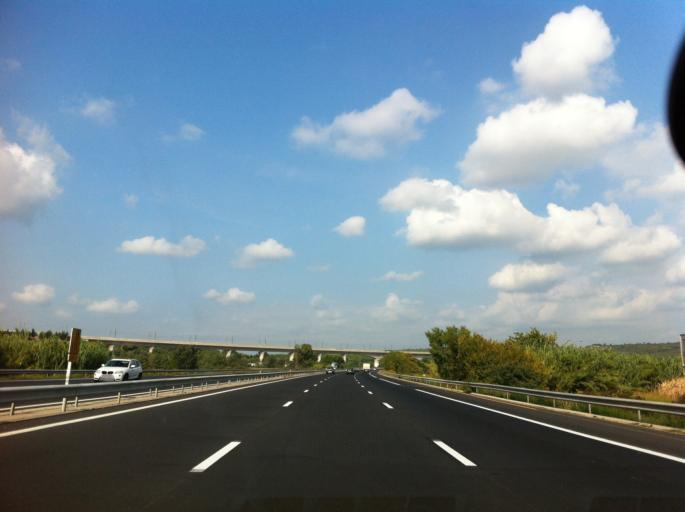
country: FR
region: Provence-Alpes-Cote d'Azur
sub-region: Departement des Bouches-du-Rhone
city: Eguilles
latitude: 43.5406
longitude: 5.3403
